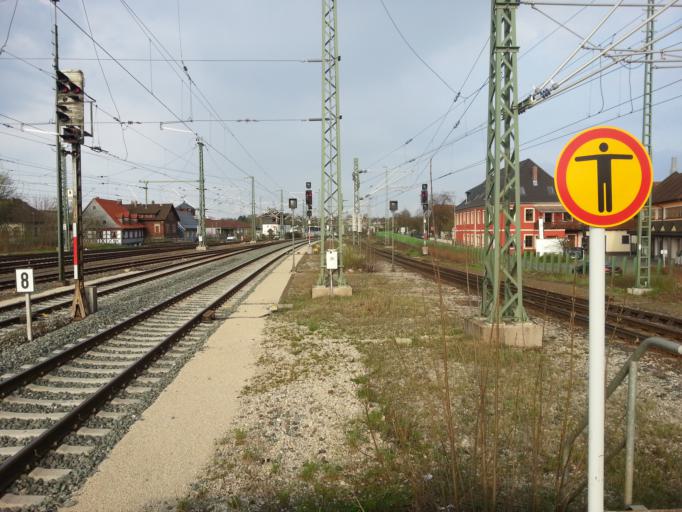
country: DE
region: Bavaria
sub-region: Upper Franconia
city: Lichtenfels
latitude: 50.1474
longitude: 11.0611
